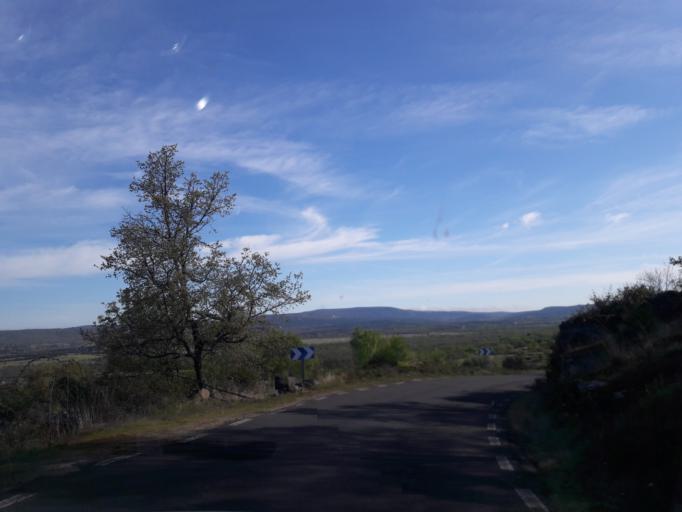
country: ES
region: Castille and Leon
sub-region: Provincia de Salamanca
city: Navalmoral de Bejar
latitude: 40.4280
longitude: -5.7828
